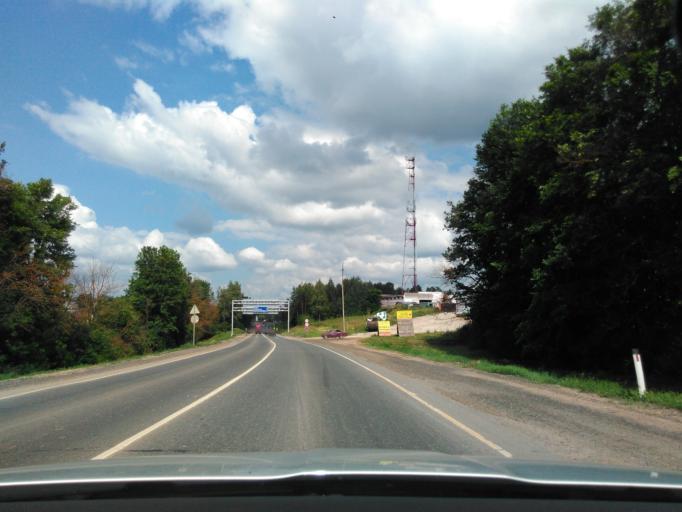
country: RU
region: Moskovskaya
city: Radumlya
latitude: 56.1032
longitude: 37.1832
